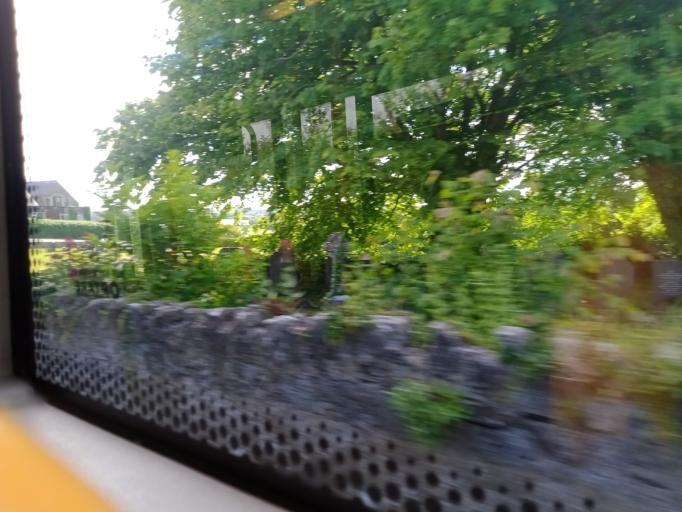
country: GB
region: Wales
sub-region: Anglesey
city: Llangoed
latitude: 53.3037
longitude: -4.0843
